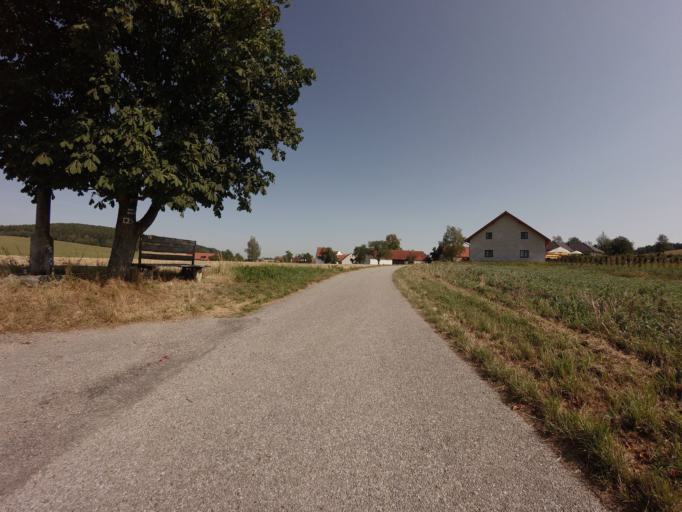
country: CZ
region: Jihocesky
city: Kamenny Ujezd
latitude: 48.8637
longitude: 14.3781
